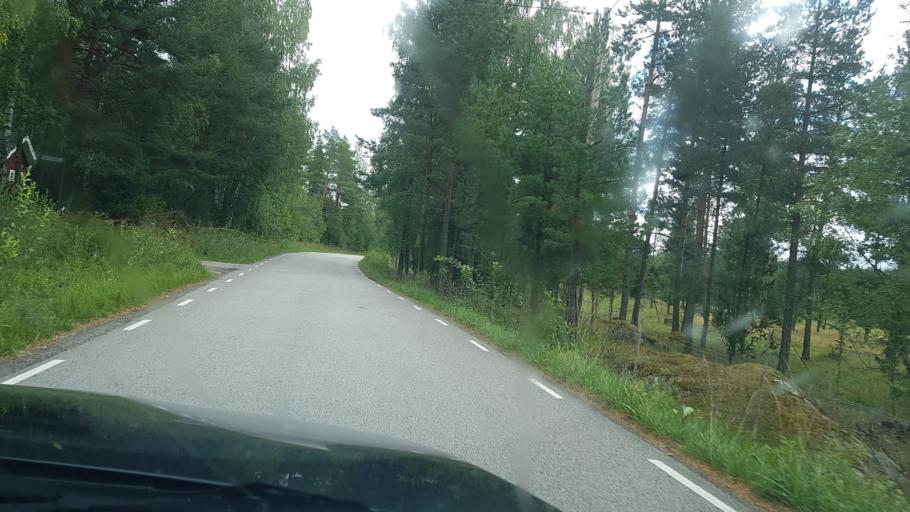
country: SE
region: Uppsala
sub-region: Osthammars Kommun
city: Oregrund
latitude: 60.3646
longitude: 18.4292
